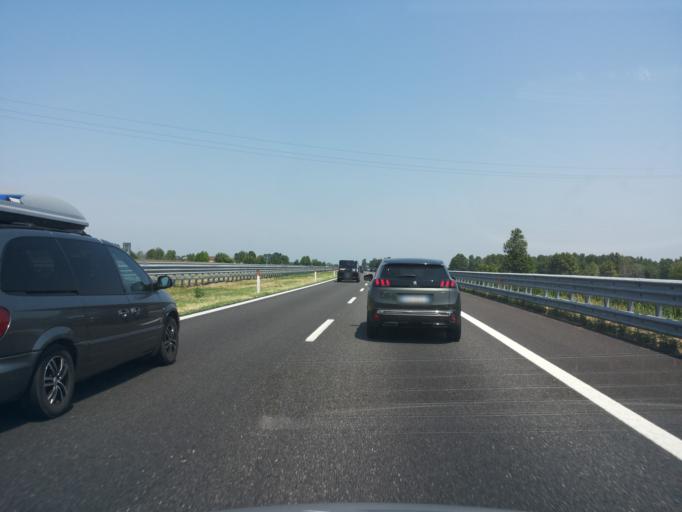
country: IT
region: Lombardy
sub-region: Provincia di Cremona
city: Corte de' Frati
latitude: 45.2224
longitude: 10.1135
